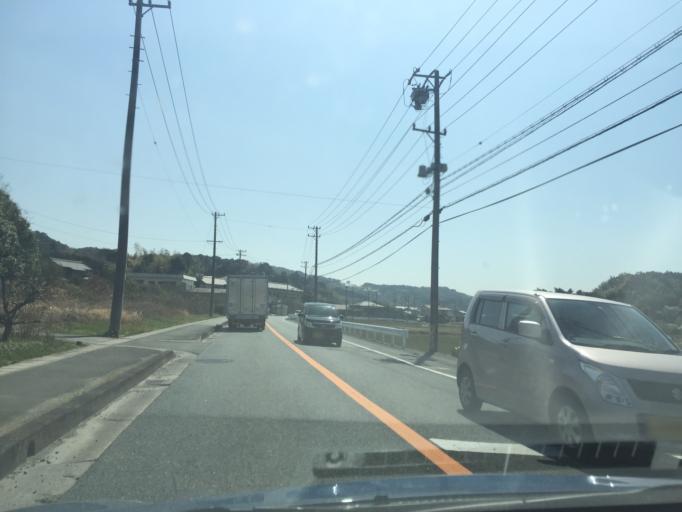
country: JP
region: Shizuoka
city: Hamamatsu
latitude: 34.7918
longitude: 137.6478
